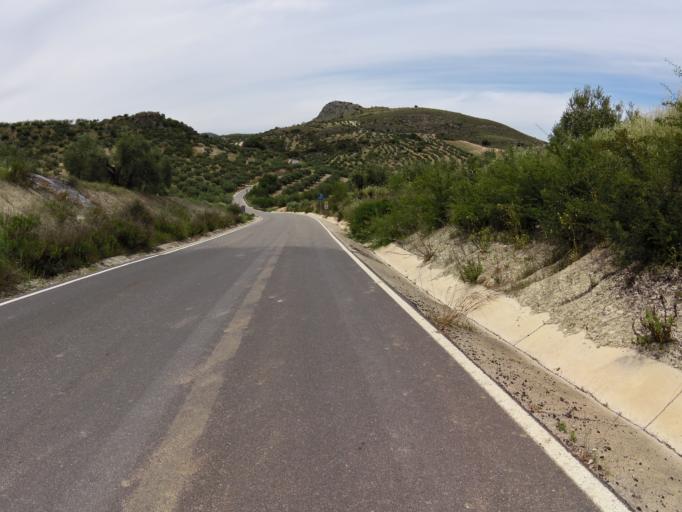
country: ES
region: Andalusia
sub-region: Province of Cordoba
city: Luque
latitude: 37.5308
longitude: -4.2532
